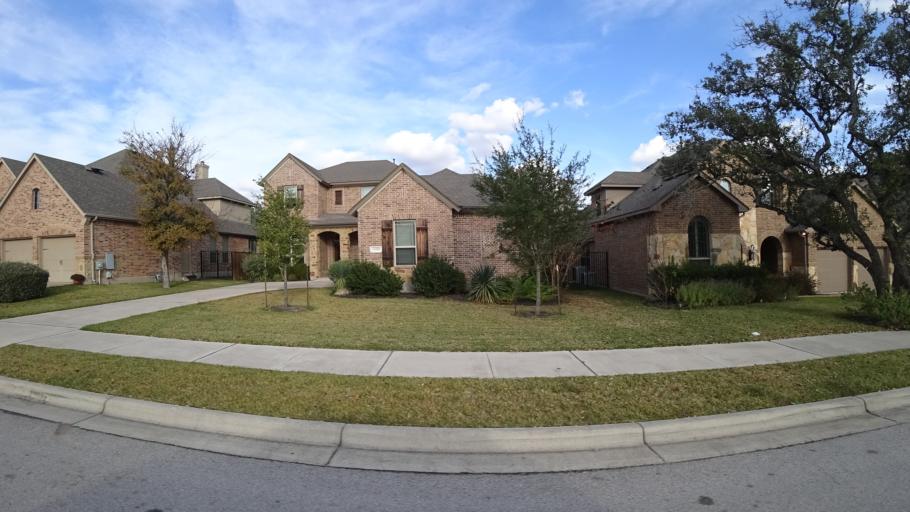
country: US
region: Texas
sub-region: Williamson County
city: Brushy Creek
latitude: 30.5053
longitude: -97.7223
